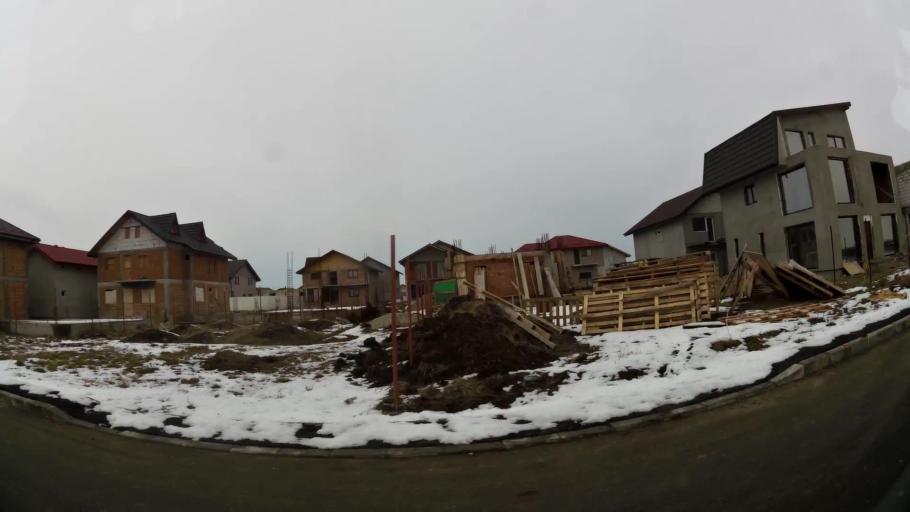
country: RO
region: Ilfov
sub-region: Comuna Tunari
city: Tunari
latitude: 44.5515
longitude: 26.1532
